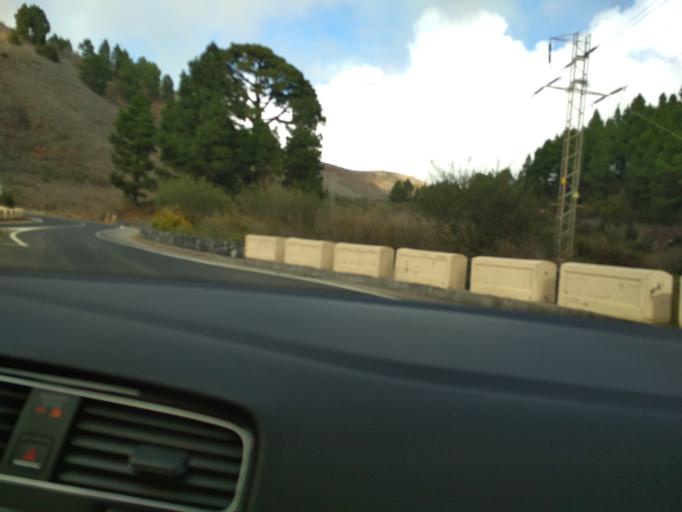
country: ES
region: Canary Islands
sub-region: Provincia de Santa Cruz de Tenerife
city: Santiago del Teide
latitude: 28.3183
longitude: -16.7970
